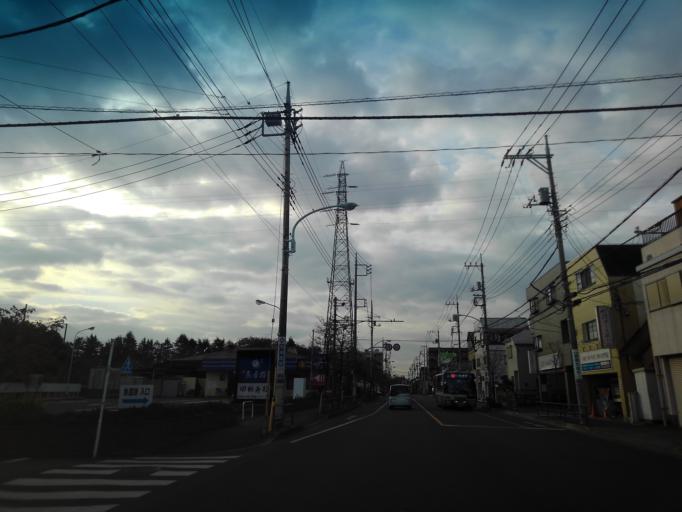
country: JP
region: Tokyo
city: Tanashicho
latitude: 35.7219
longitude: 139.5098
